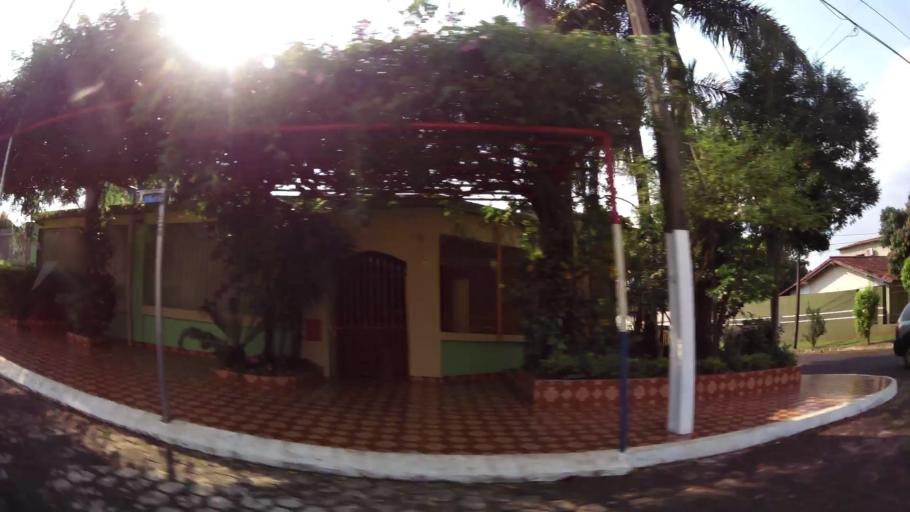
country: PY
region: Alto Parana
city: Presidente Franco
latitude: -25.5276
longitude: -54.6244
